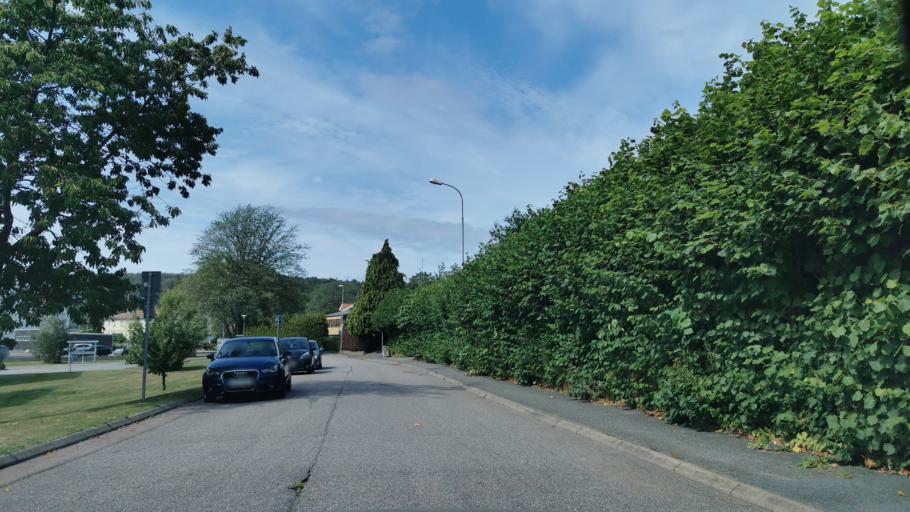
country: SE
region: Vaestra Goetaland
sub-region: Molndal
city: Moelndal
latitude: 57.6634
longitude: 12.0010
